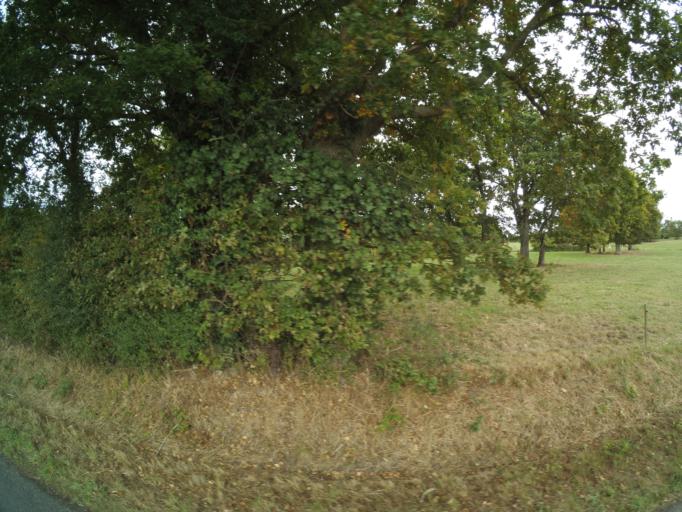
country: FR
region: Pays de la Loire
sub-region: Departement de la Loire-Atlantique
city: Remouille
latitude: 47.0507
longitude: -1.3454
